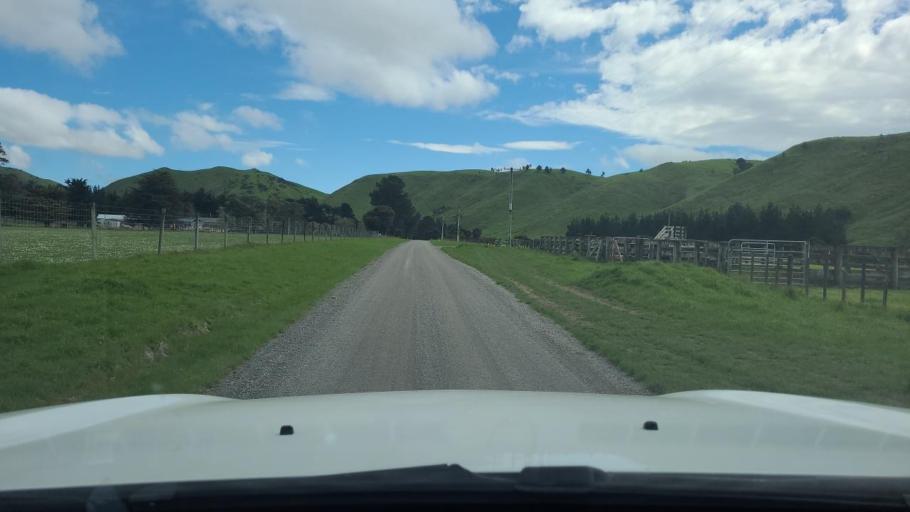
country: NZ
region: Wellington
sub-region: South Wairarapa District
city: Waipawa
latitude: -41.3215
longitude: 175.4165
